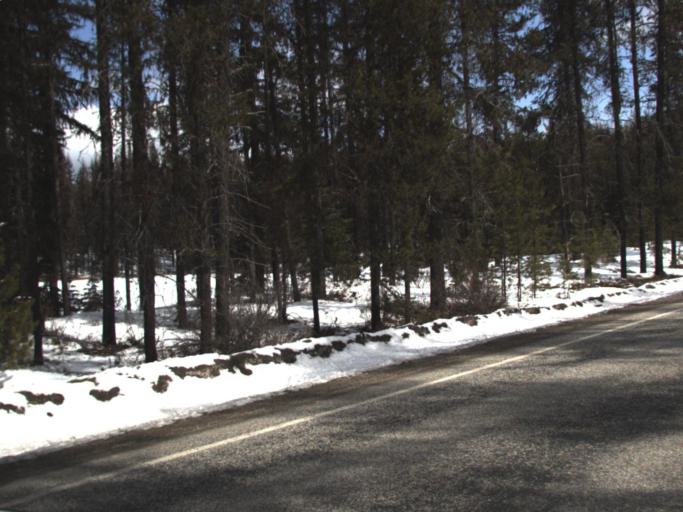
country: US
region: Washington
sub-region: Stevens County
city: Colville
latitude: 48.6545
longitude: -117.4834
